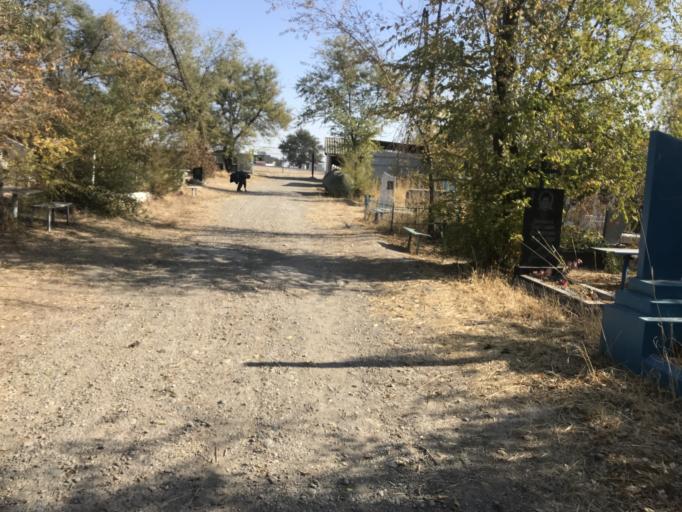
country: KZ
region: Ongtustik Qazaqstan
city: Aksu
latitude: 42.4202
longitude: 69.8032
